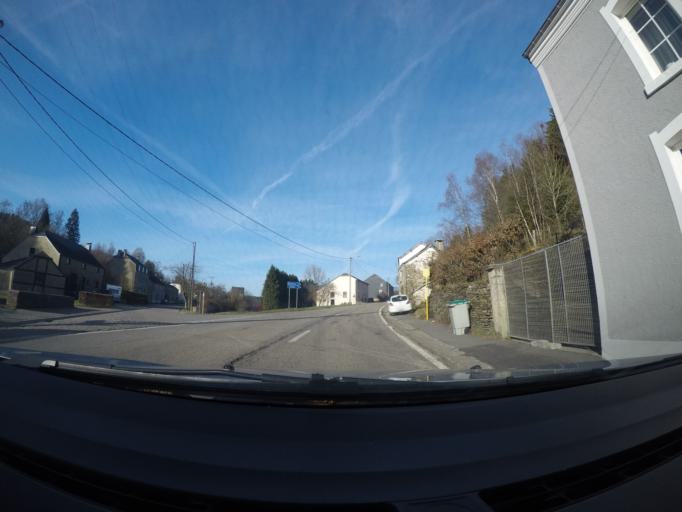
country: BE
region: Wallonia
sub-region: Province du Luxembourg
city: Leglise
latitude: 49.7645
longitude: 5.5135
